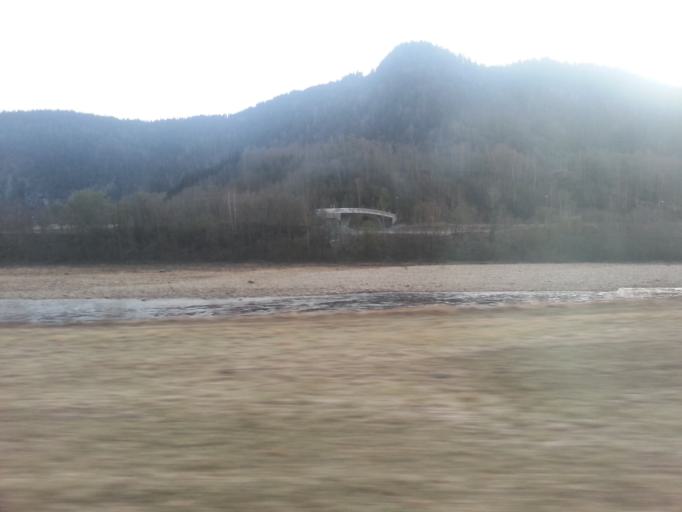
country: NO
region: Sor-Trondelag
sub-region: Midtre Gauldal
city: Storen
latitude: 63.0687
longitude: 10.2672
